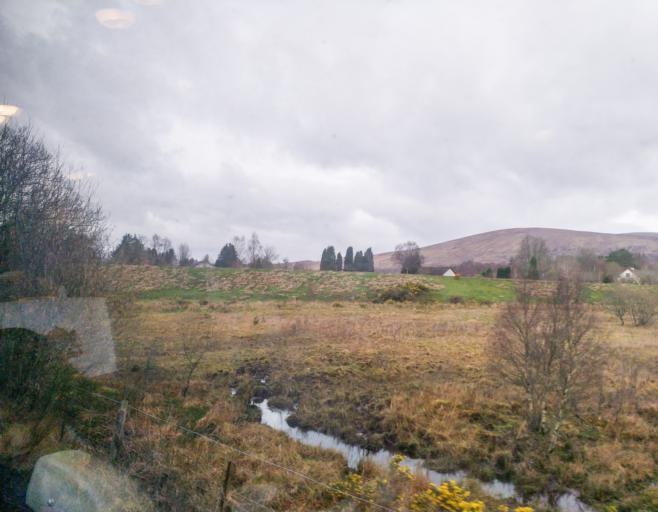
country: GB
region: Scotland
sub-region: Highland
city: Spean Bridge
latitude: 56.8881
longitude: -4.8568
